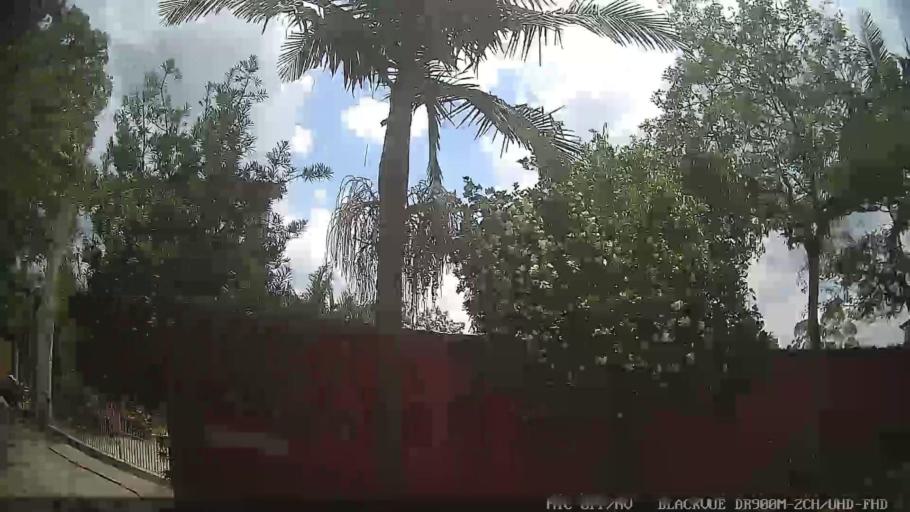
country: BR
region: Sao Paulo
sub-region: Ferraz De Vasconcelos
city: Ferraz de Vasconcelos
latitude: -23.5867
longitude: -46.3601
